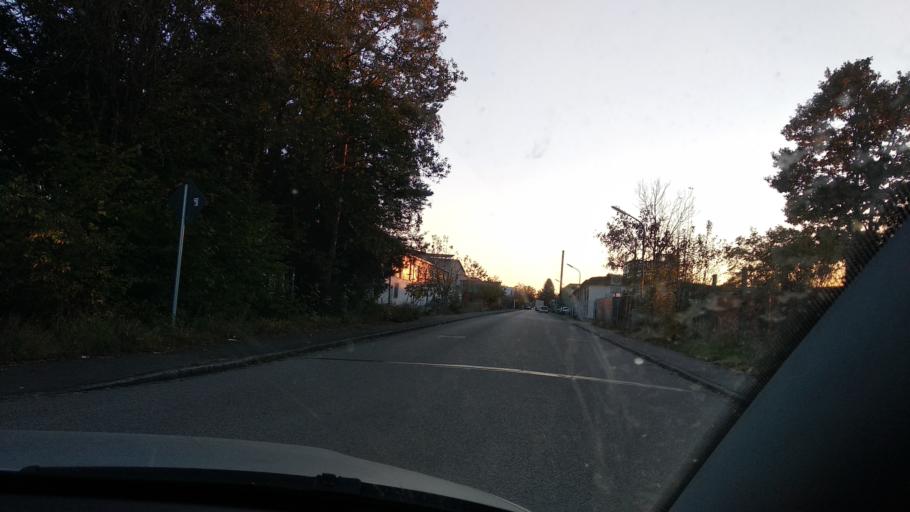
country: DE
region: Bavaria
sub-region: Upper Bavaria
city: Hohenbrunn
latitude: 48.0418
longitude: 11.7223
